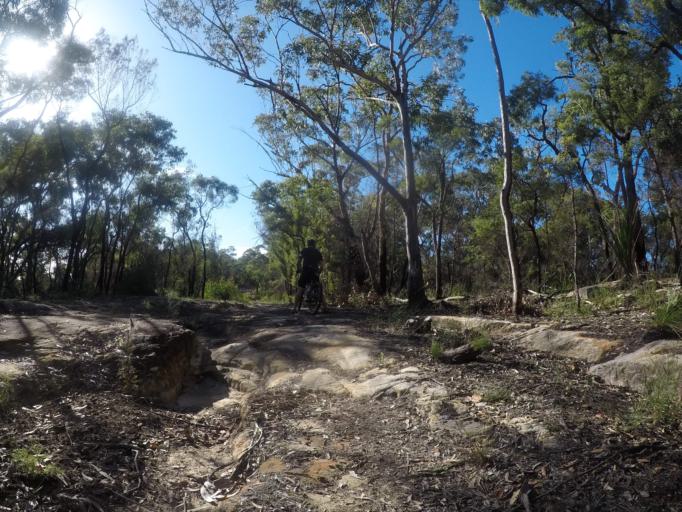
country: AU
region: New South Wales
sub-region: Hornsby Shire
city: Glenorie
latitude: -33.3423
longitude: 151.0591
